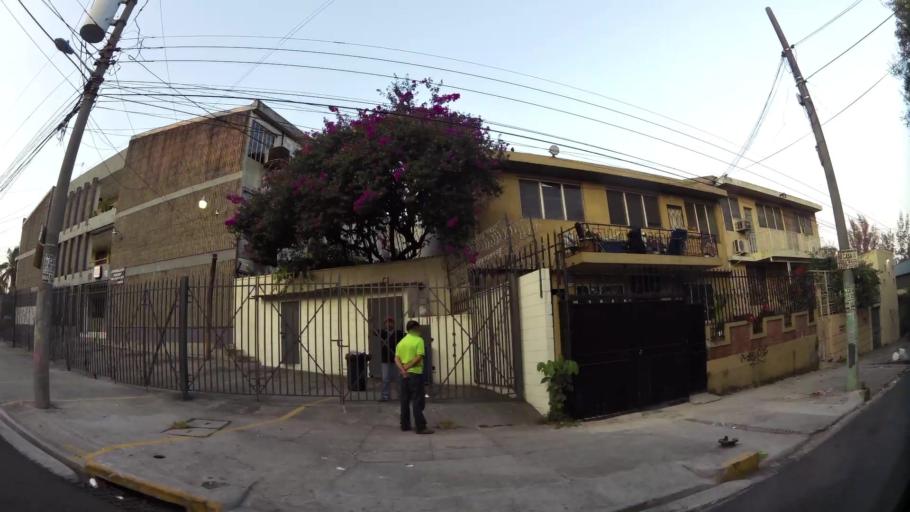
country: SV
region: San Salvador
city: Mejicanos
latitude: 13.7120
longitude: -89.2057
